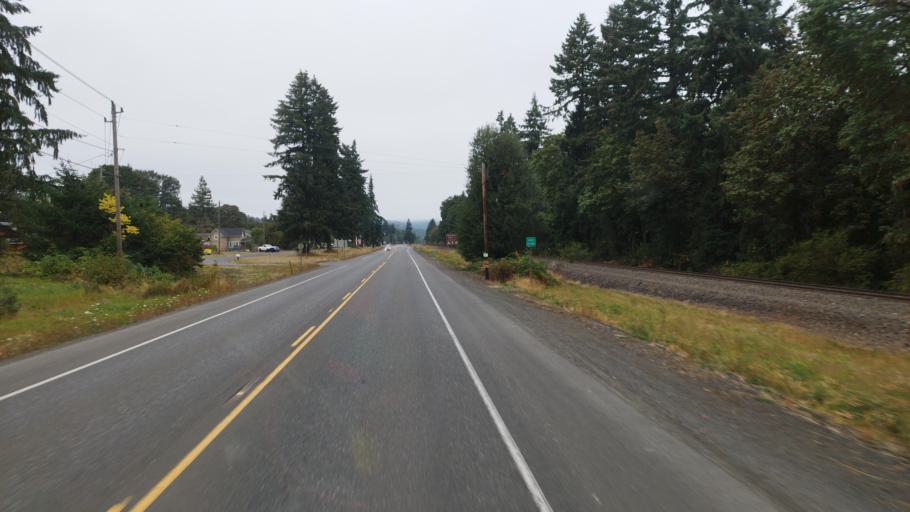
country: US
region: Oregon
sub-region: Columbia County
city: Columbia City
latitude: 45.9291
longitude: -122.8410
